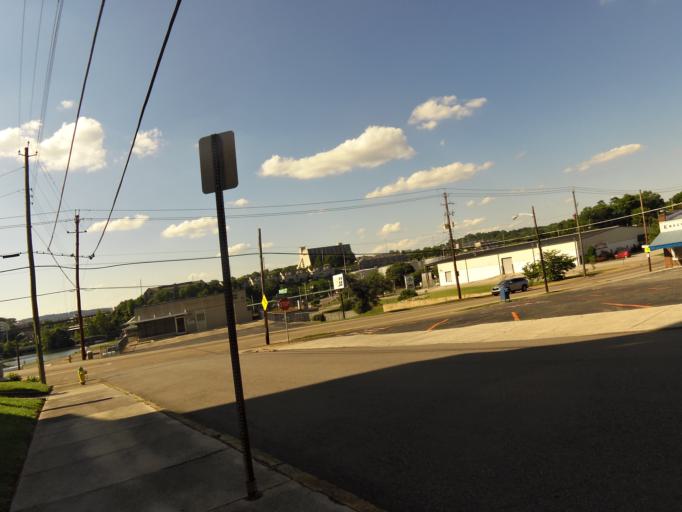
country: US
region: Tennessee
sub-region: Knox County
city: Knoxville
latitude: 35.9567
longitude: -83.9101
